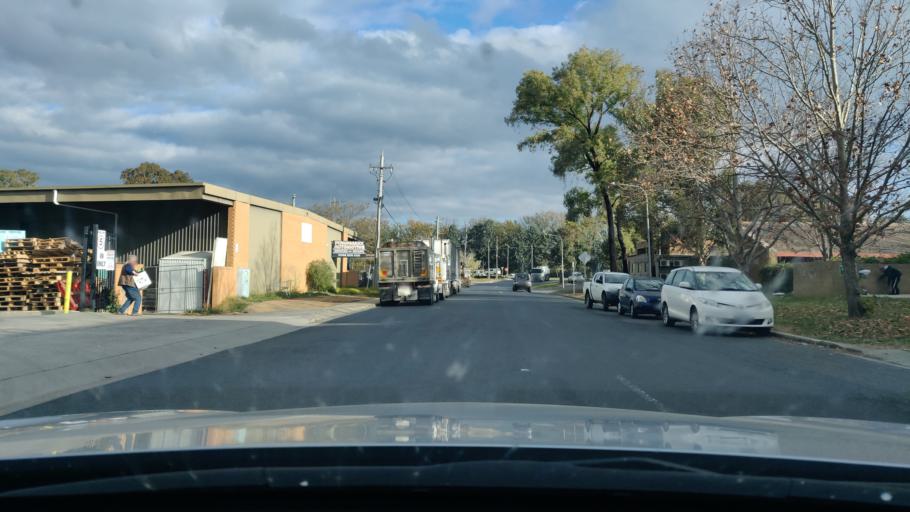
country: AU
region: Australian Capital Territory
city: Forrest
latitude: -35.3238
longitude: 149.1540
